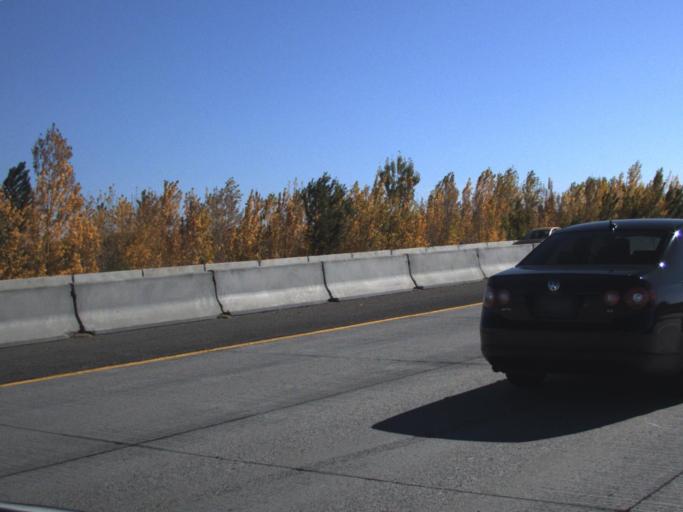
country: US
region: Washington
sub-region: Benton County
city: Richland
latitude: 46.2452
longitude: -119.2501
